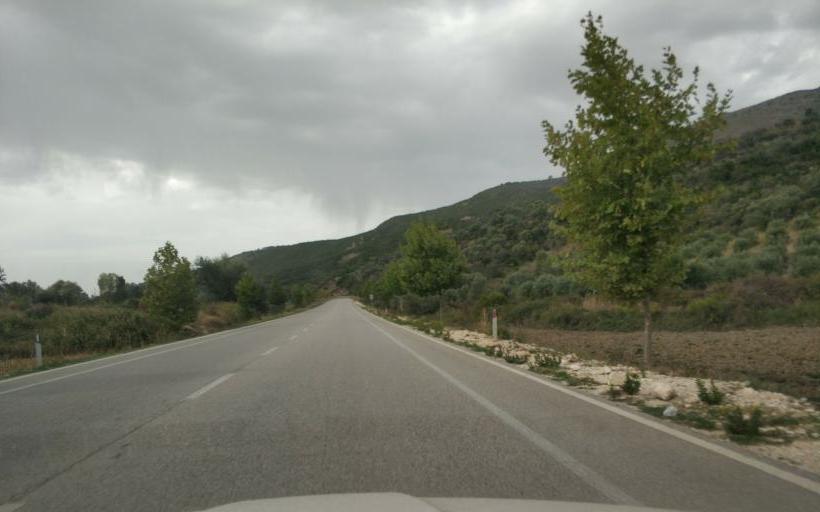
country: AL
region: Fier
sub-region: Rrethi i Mallakastres
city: Hekal
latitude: 40.5214
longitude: 19.7404
